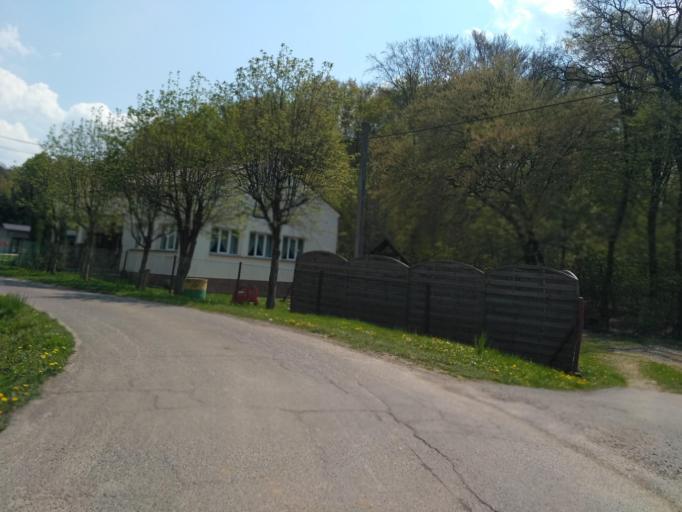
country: PL
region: Subcarpathian Voivodeship
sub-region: Powiat jasielski
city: Tarnowiec
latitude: 49.7422
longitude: 21.5898
